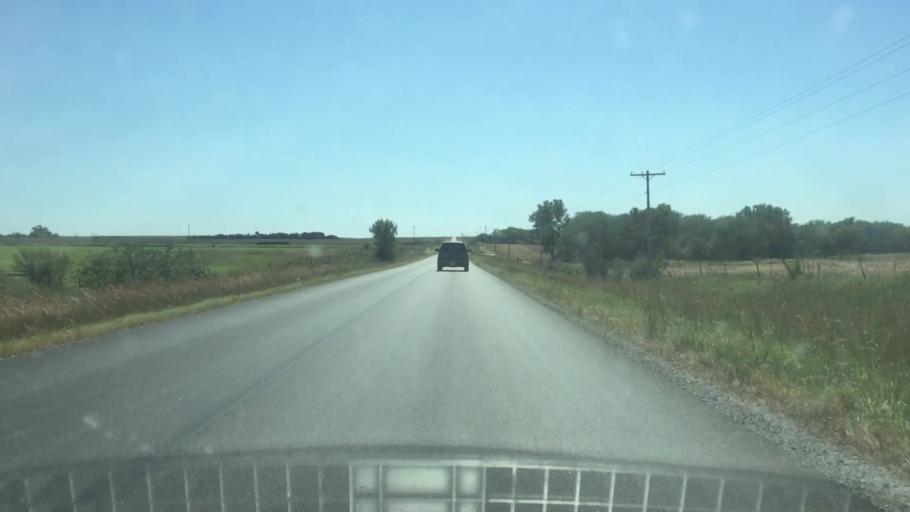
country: US
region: Kansas
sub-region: Marshall County
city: Marysville
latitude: 39.8834
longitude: -96.6010
